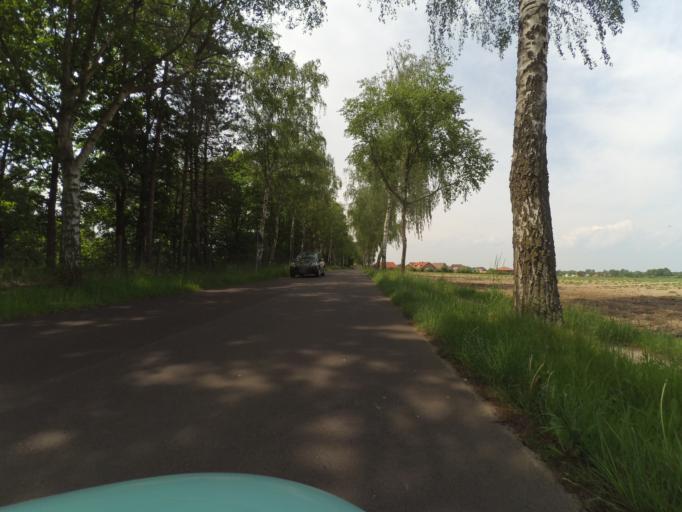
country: DE
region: Lower Saxony
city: Peine
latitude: 52.3482
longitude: 10.1918
